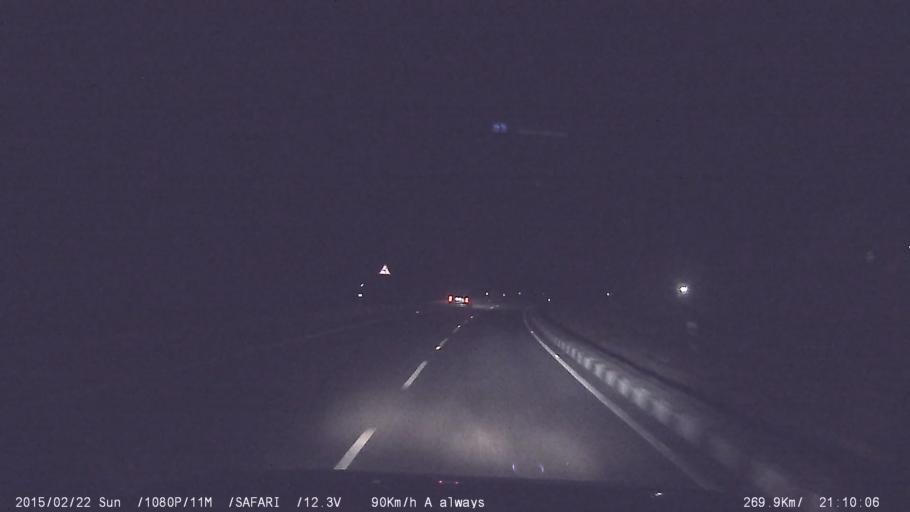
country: IN
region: Tamil Nadu
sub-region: Karur
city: Pallappatti
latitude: 10.7549
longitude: 77.9120
